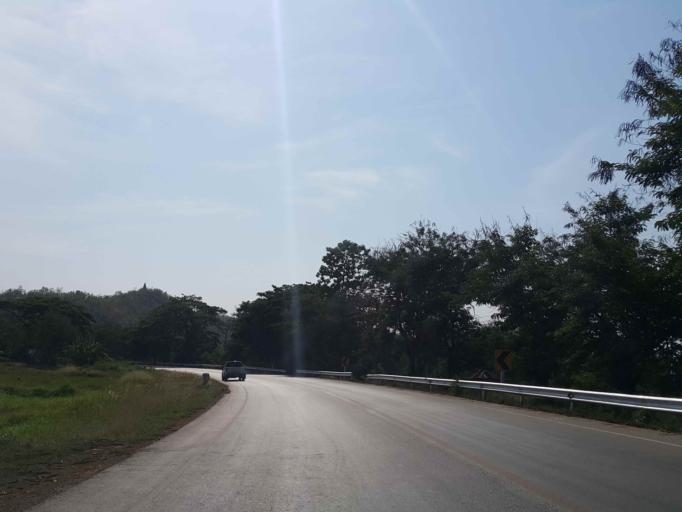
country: TH
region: Sukhothai
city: Thung Saliam
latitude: 17.3438
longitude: 99.5979
